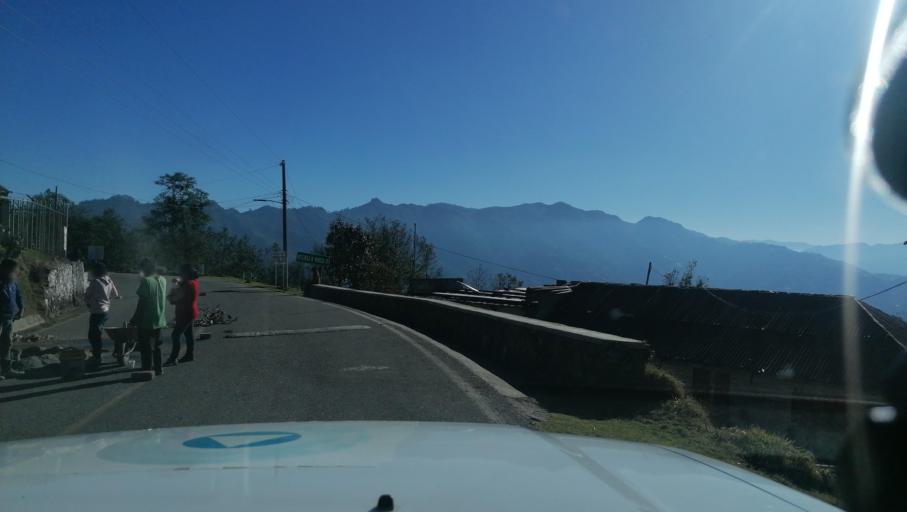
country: MX
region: Chiapas
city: Motozintla de Mendoza
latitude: 15.2380
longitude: -92.2316
